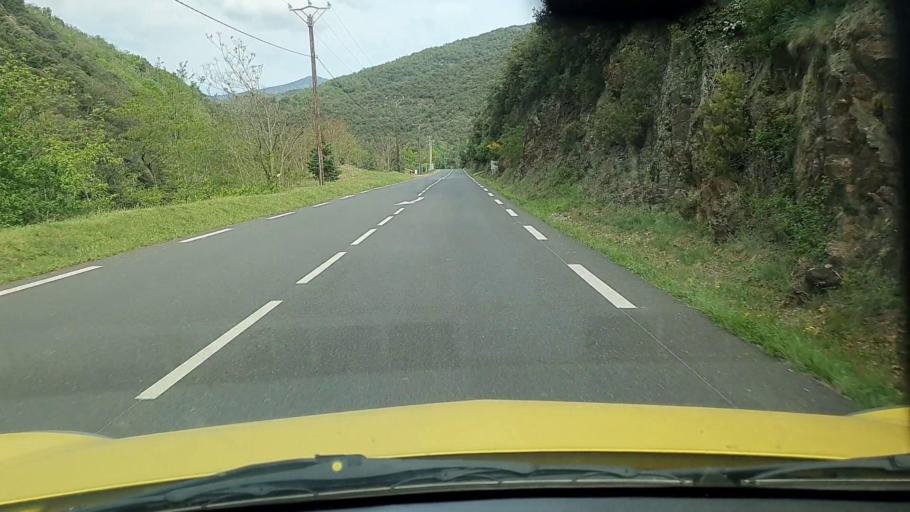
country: FR
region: Languedoc-Roussillon
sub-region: Departement du Gard
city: Valleraugue
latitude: 44.0747
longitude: 3.6697
